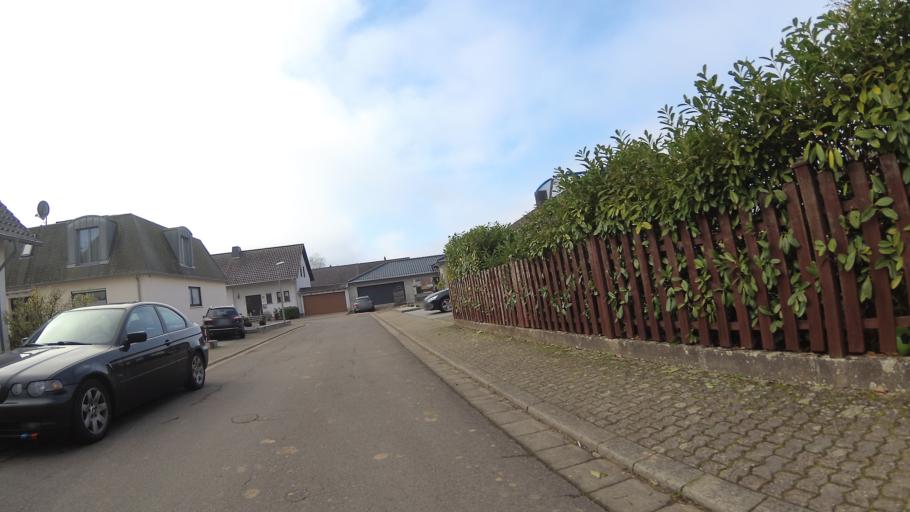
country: DE
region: Saarland
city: Ensdorf
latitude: 49.3020
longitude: 6.7868
